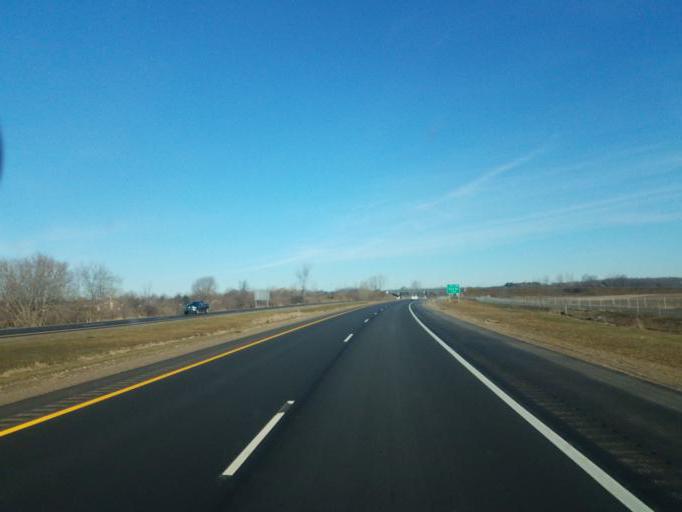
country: US
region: Michigan
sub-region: Gratiot County
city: Ithaca
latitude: 43.3033
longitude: -84.5937
